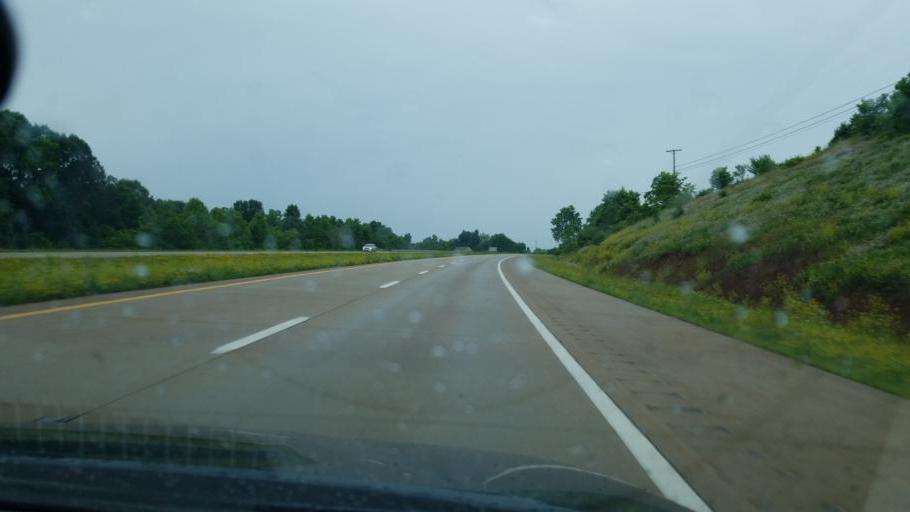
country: US
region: West Virginia
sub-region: Wood County
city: Washington
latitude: 39.2331
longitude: -81.8825
